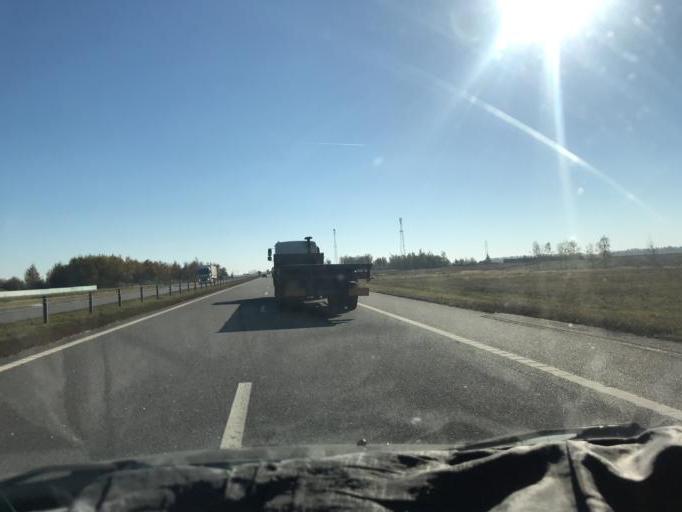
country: BY
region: Mogilev
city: Yalizava
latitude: 53.2515
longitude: 28.9220
